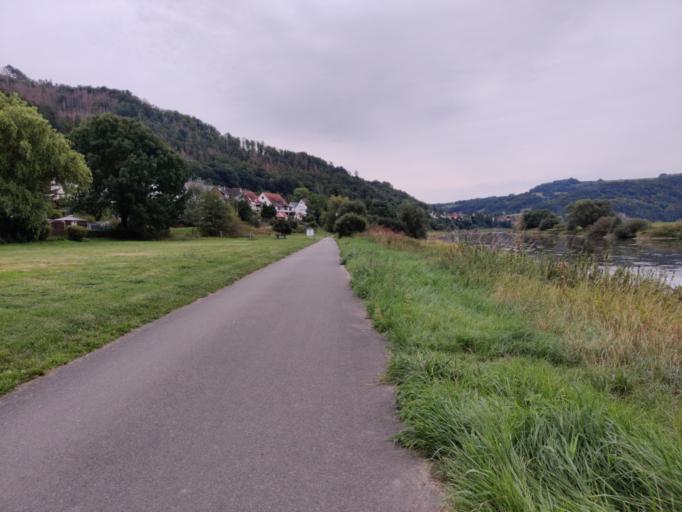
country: DE
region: Lower Saxony
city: Pegestorf
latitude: 51.9398
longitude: 9.5100
